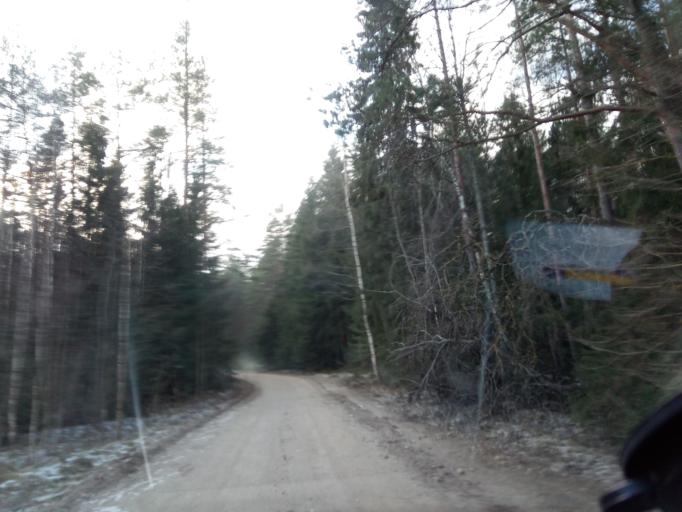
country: LT
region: Alytaus apskritis
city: Varena
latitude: 53.9853
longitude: 24.3371
